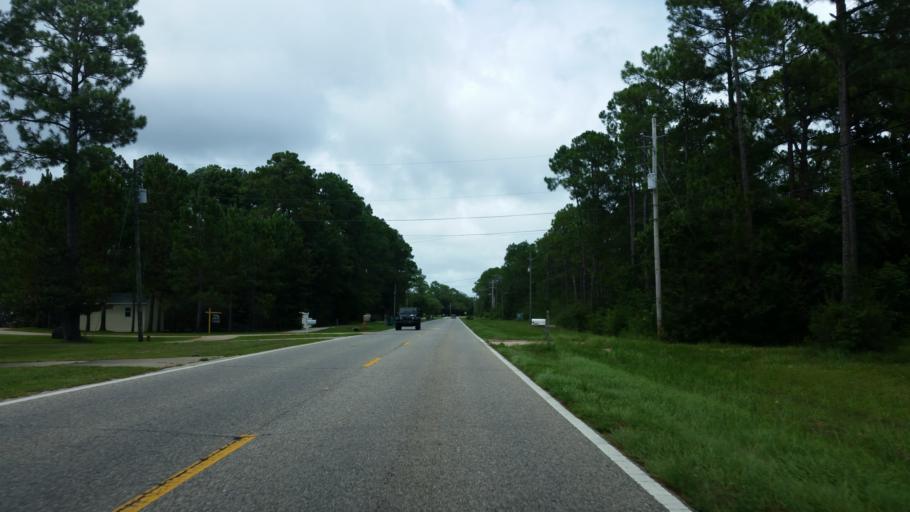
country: US
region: Florida
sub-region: Santa Rosa County
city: Holley
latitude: 30.4426
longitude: -86.9501
